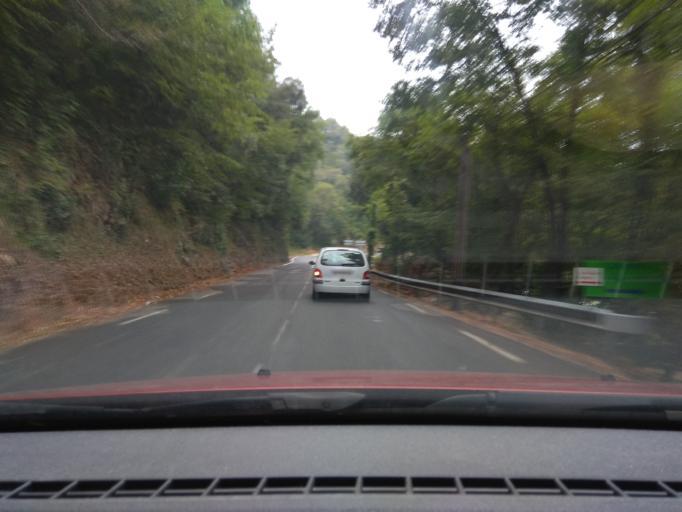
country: FR
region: Provence-Alpes-Cote d'Azur
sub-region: Departement des Alpes-Maritimes
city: La Colle-sur-Loup
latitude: 43.6830
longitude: 7.0745
